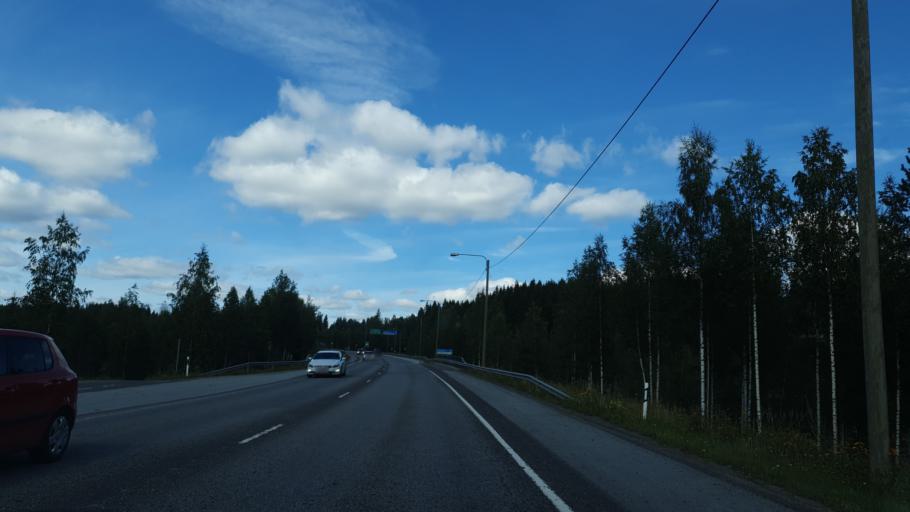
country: FI
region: Central Finland
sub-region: Jyvaeskylae
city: Muurame
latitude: 62.1632
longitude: 25.6816
